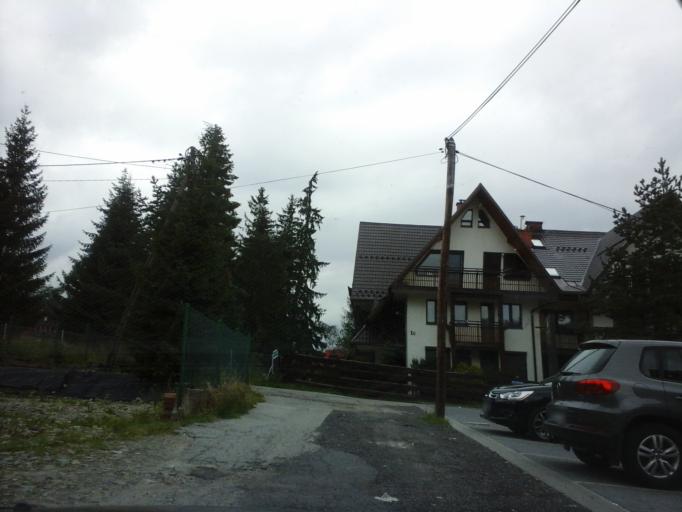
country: PL
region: Lesser Poland Voivodeship
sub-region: Powiat tatrzanski
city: Zakopane
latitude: 49.2854
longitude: 19.9912
